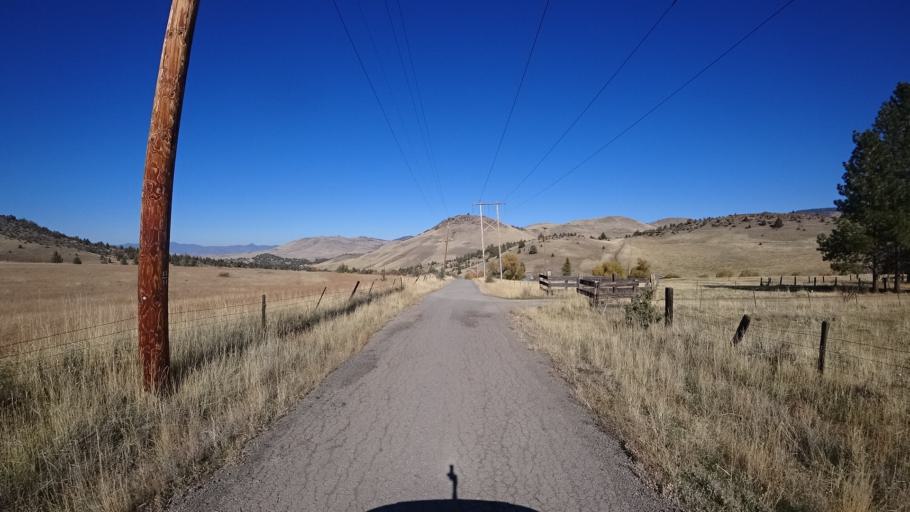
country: US
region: California
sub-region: Siskiyou County
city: Montague
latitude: 41.7838
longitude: -122.3590
